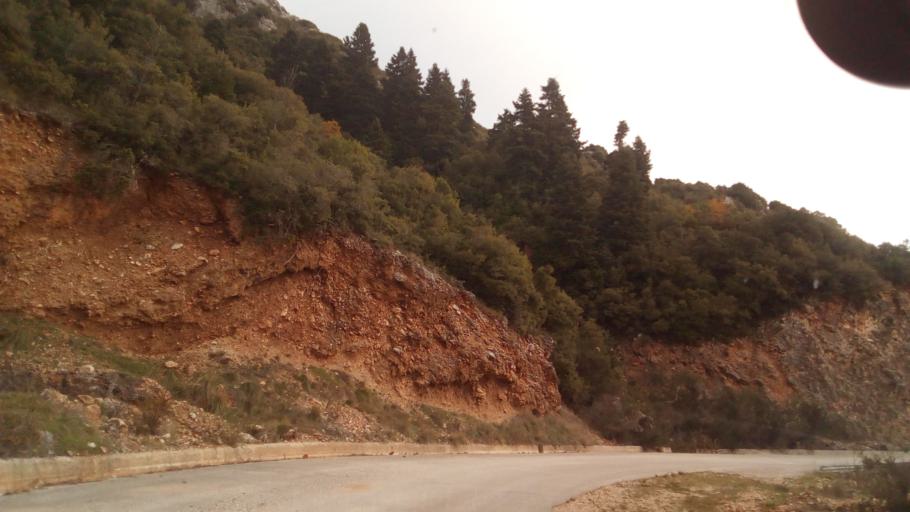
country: GR
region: West Greece
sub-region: Nomos Aitolias kai Akarnanias
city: Thermo
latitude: 38.6810
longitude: 21.8757
